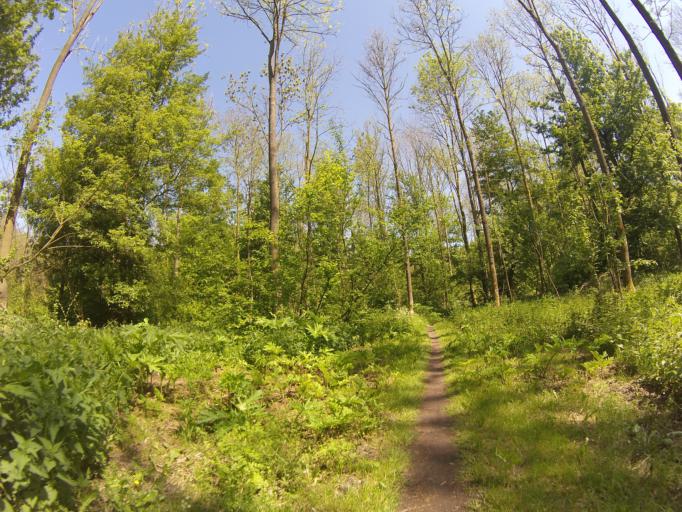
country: NL
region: Flevoland
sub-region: Gemeente Zeewolde
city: Zeewolde
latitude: 52.2940
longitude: 5.5226
